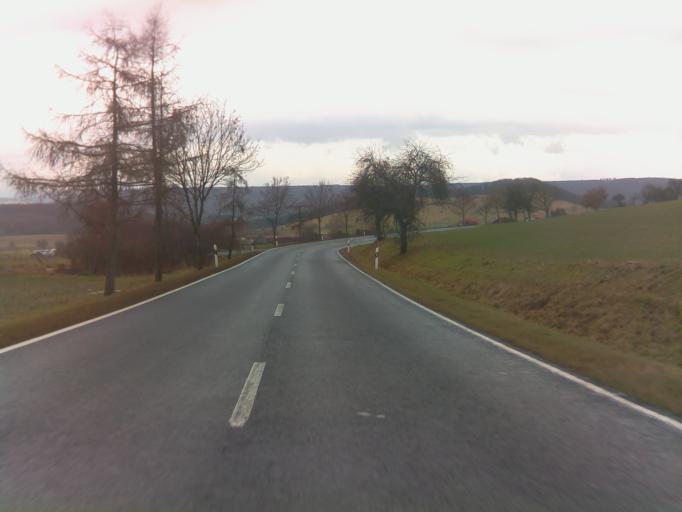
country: DE
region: Thuringia
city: Stepfershausen
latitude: 50.6022
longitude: 10.2883
